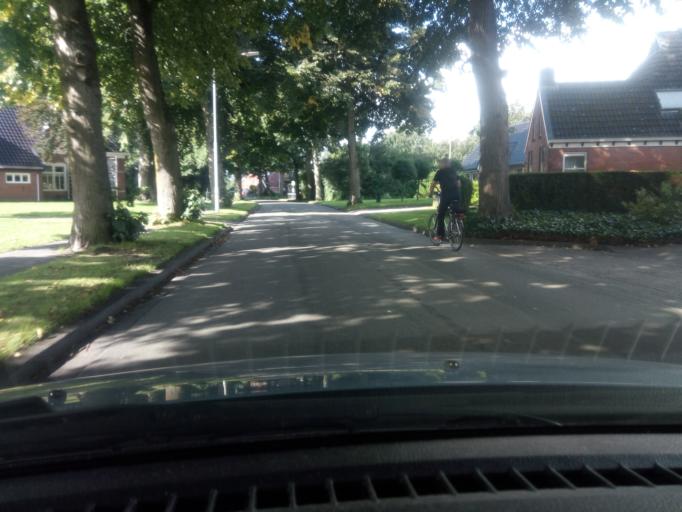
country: NL
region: Friesland
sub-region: Gemeente Achtkarspelen
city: Surhuisterveen
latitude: 53.1855
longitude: 6.1762
